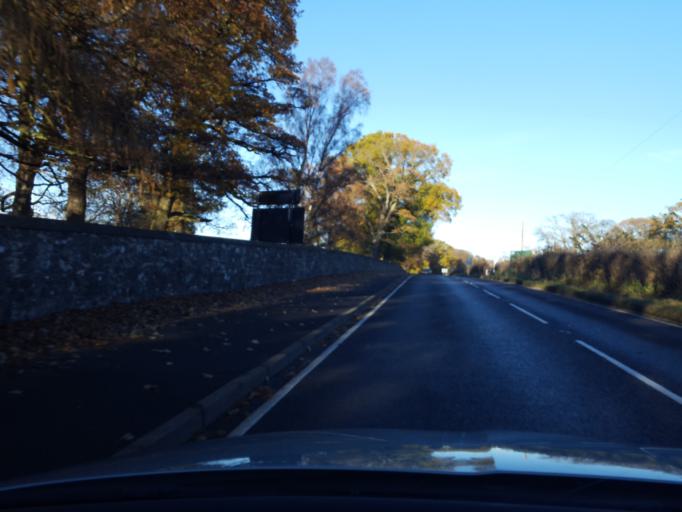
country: GB
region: Scotland
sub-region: Perth and Kinross
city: Perth
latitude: 56.4142
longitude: -3.4283
